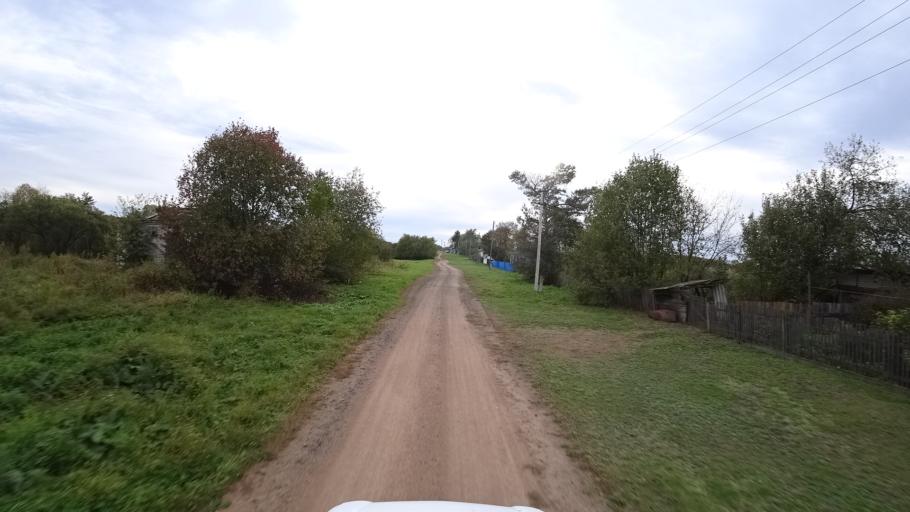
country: RU
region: Amur
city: Arkhara
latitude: 49.4342
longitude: 130.2645
